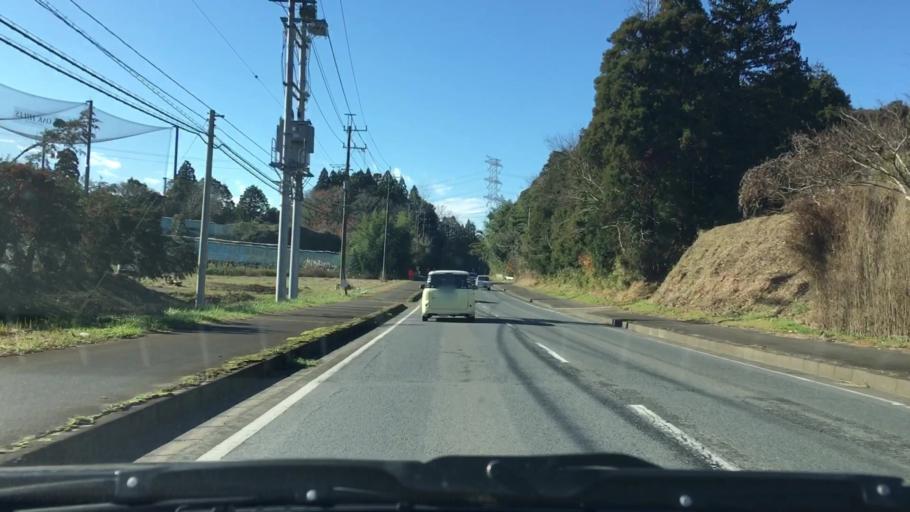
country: JP
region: Chiba
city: Sawara
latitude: 35.8095
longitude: 140.4897
